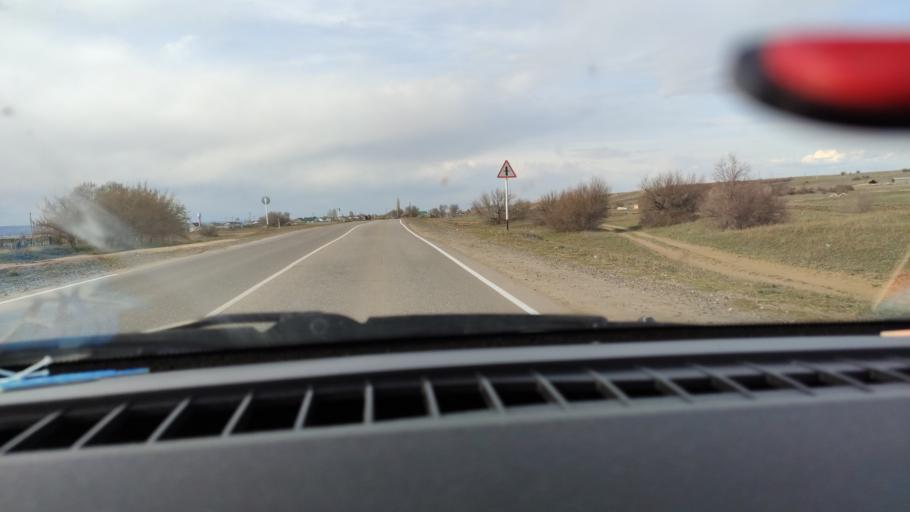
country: RU
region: Saratov
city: Privolzhskiy
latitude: 51.1980
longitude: 45.9158
